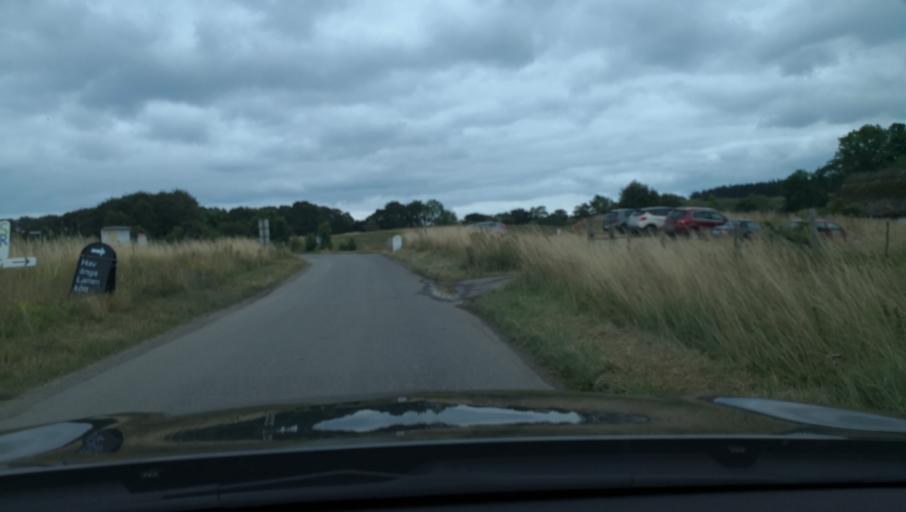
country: SE
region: Skane
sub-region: Simrishamns Kommun
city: Kivik
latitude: 55.7242
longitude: 14.1861
